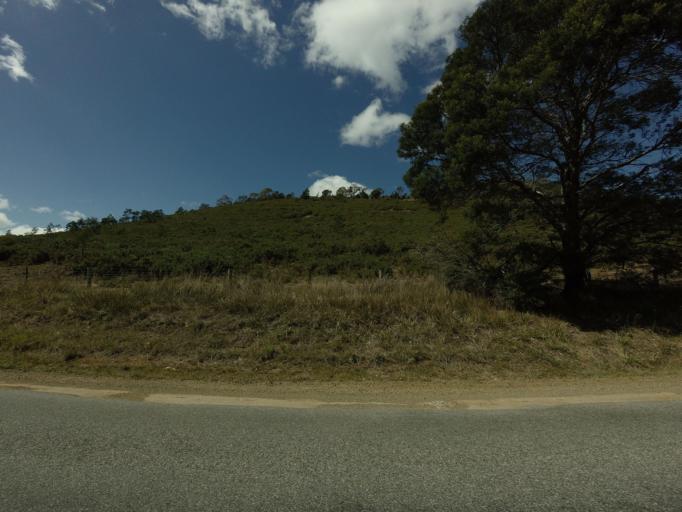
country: AU
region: Tasmania
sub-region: Break O'Day
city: St Helens
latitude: -41.9583
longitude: 148.1619
